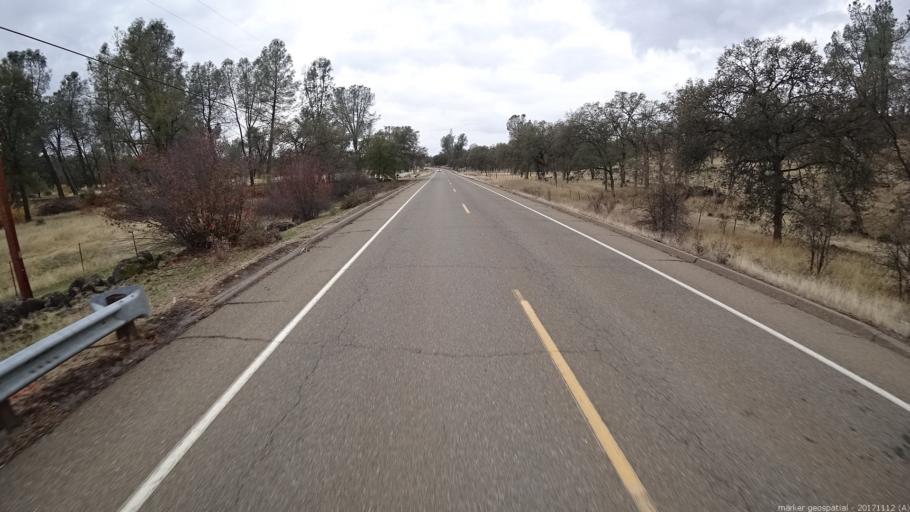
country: US
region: California
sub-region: Shasta County
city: Palo Cedro
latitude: 40.4881
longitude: -122.1357
